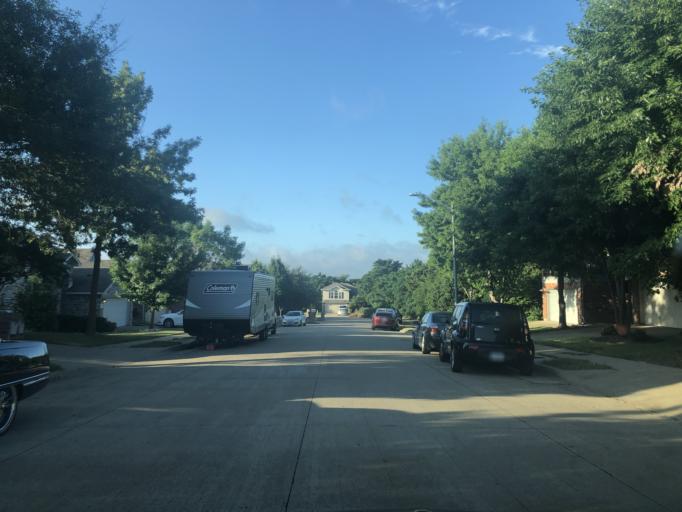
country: US
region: Texas
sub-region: Dallas County
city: Duncanville
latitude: 32.6630
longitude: -96.9512
